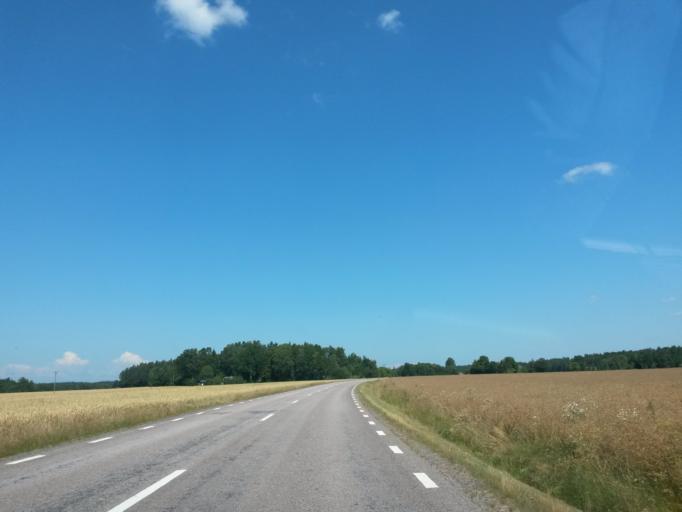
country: SE
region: Vaestra Goetaland
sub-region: Grastorps Kommun
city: Graestorp
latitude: 58.3106
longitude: 12.6695
